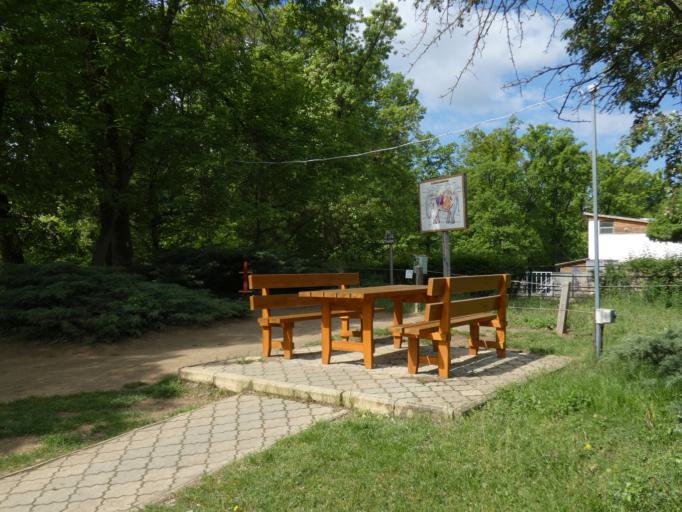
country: HU
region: Szabolcs-Szatmar-Bereg
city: Nyiregyhaza
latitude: 47.9984
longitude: 21.7266
